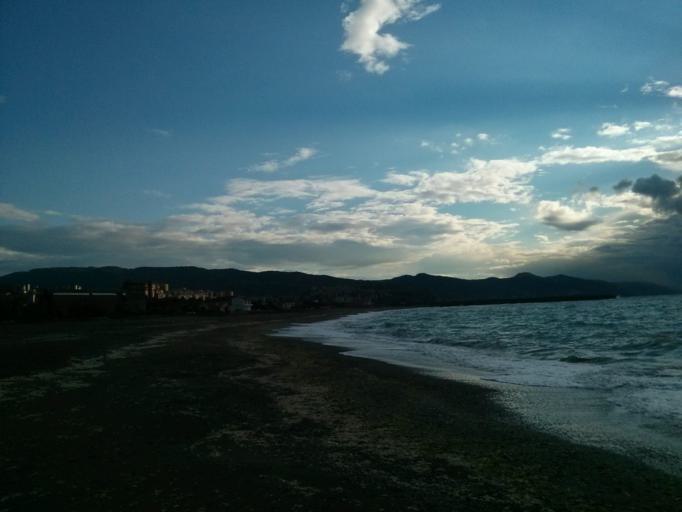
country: TR
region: Zonguldak
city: Tieum
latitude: 41.5705
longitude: 32.0288
